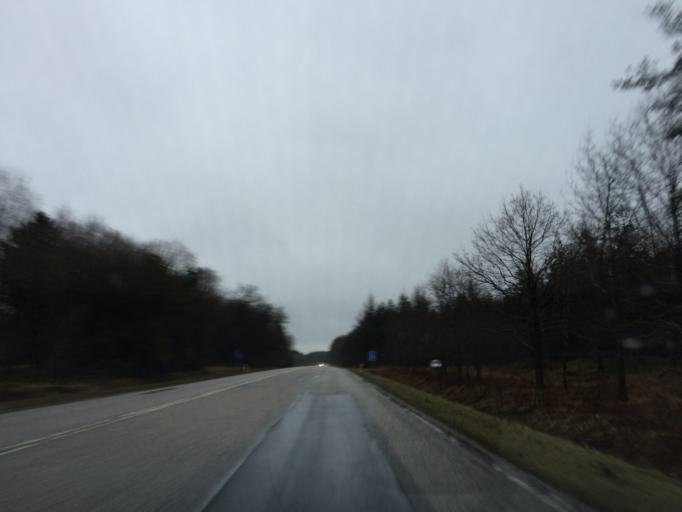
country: DK
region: North Denmark
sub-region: Mariagerfjord Kommune
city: Arden
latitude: 56.8160
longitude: 9.8197
